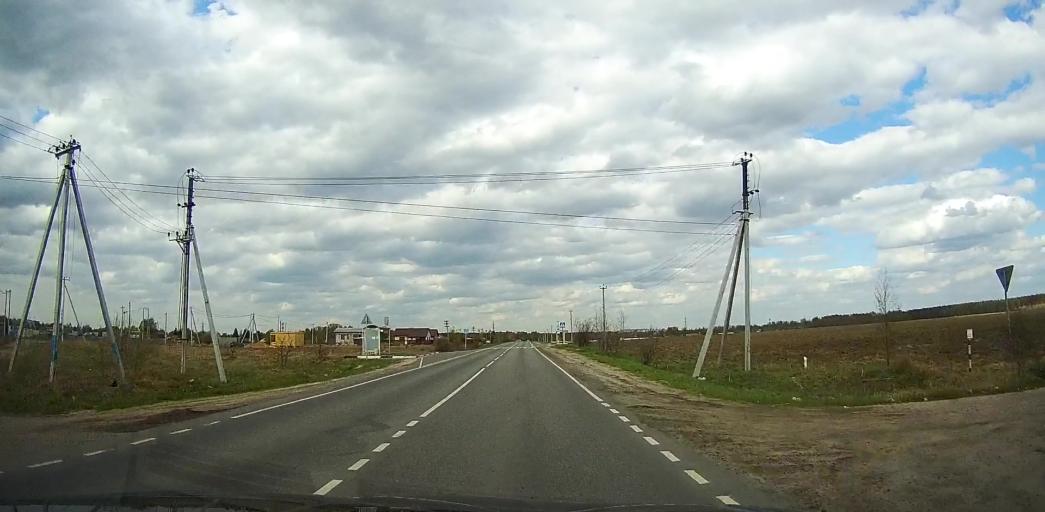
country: RU
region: Moskovskaya
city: Pavlovskiy Posad
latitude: 55.7452
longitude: 38.6491
